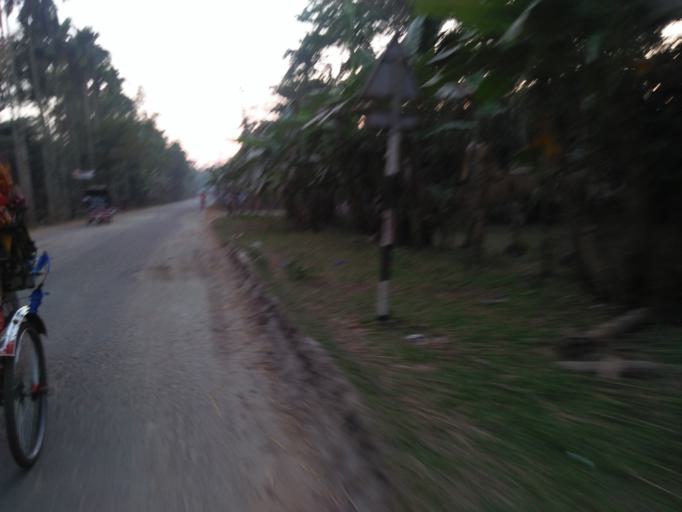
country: BD
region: Barisal
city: Bhola
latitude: 22.7550
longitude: 90.6363
